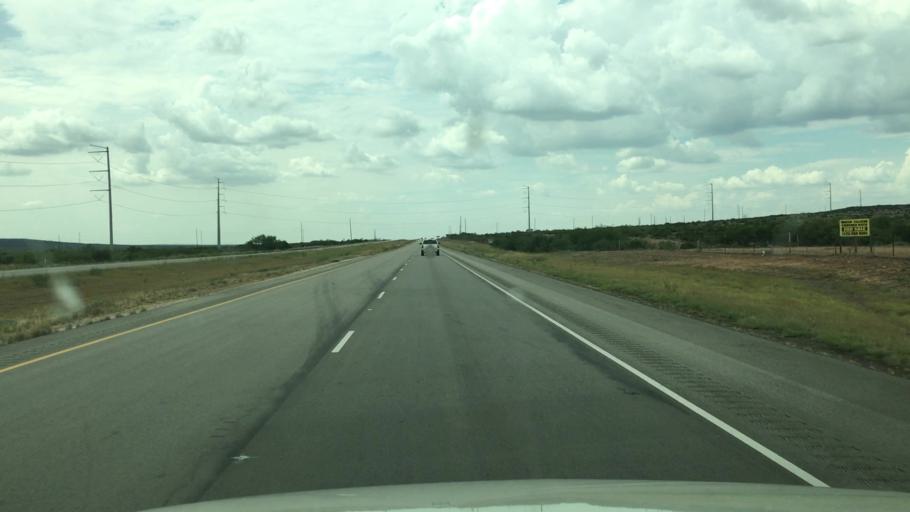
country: US
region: Texas
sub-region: Glasscock County
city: Garden City
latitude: 31.9844
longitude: -101.2598
